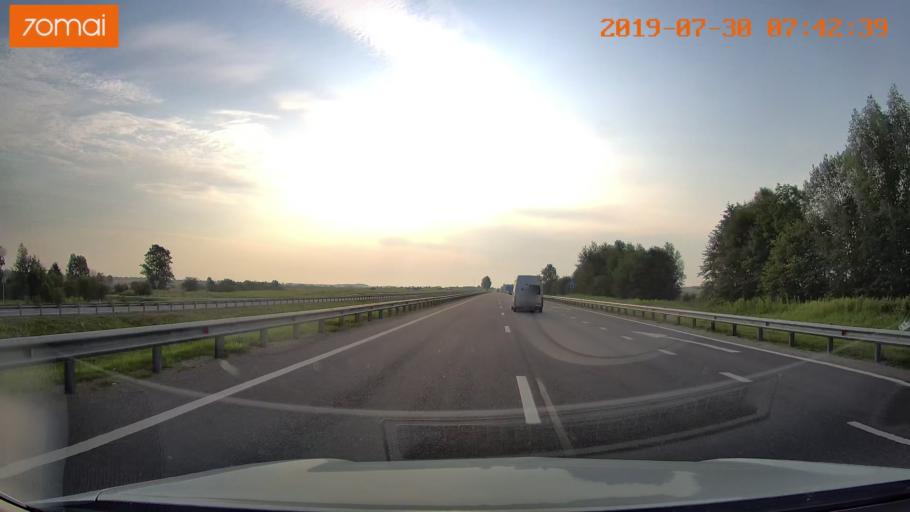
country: RU
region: Kaliningrad
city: Gvardeysk
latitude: 54.6480
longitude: 21.2847
